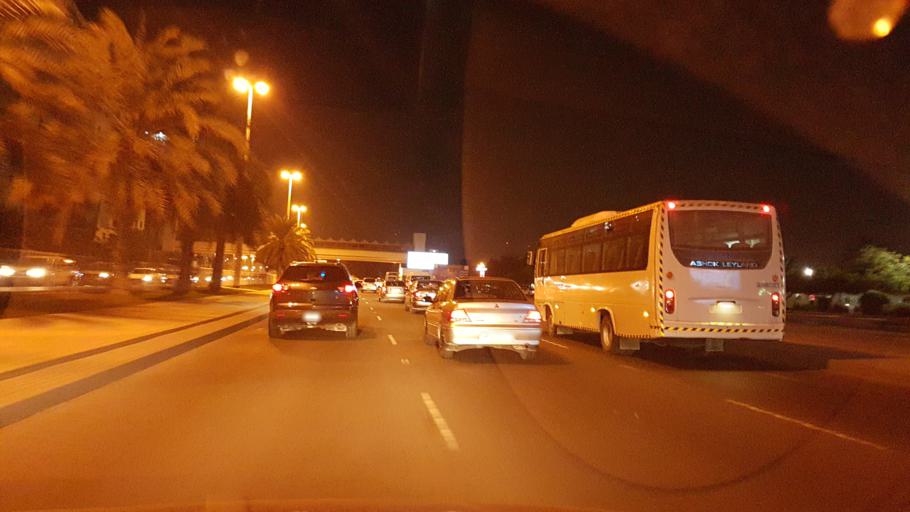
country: BH
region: Manama
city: Manama
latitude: 26.2305
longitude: 50.5990
